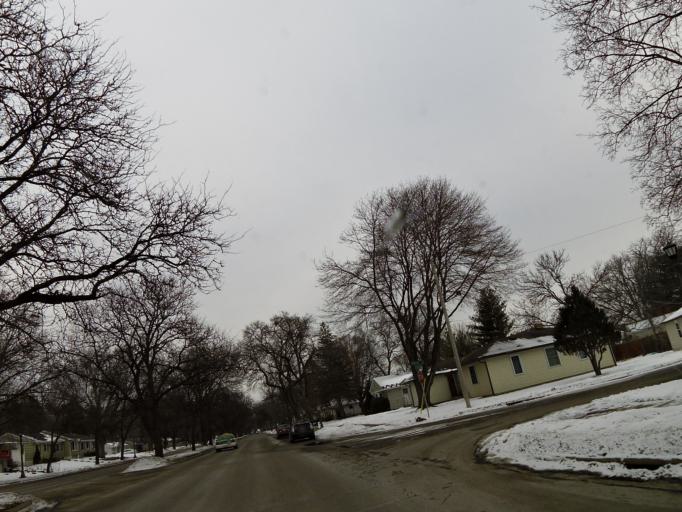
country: US
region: Minnesota
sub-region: Dakota County
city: Mendota Heights
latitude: 44.9092
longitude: -93.1826
